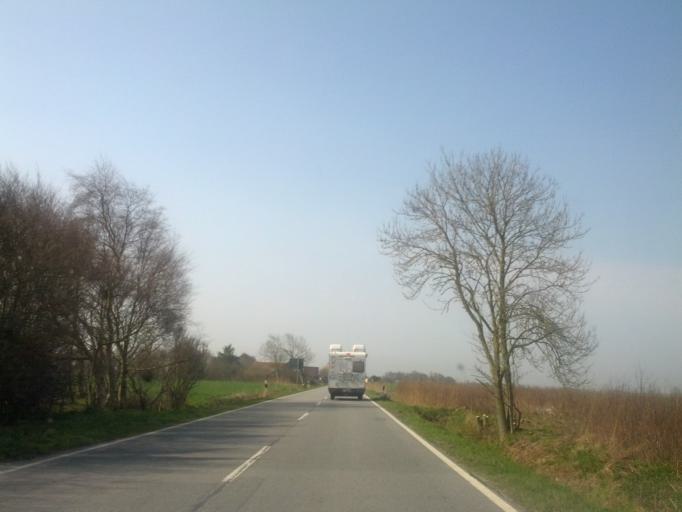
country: DE
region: Lower Saxony
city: Hagermarsch
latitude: 53.6592
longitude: 7.2864
